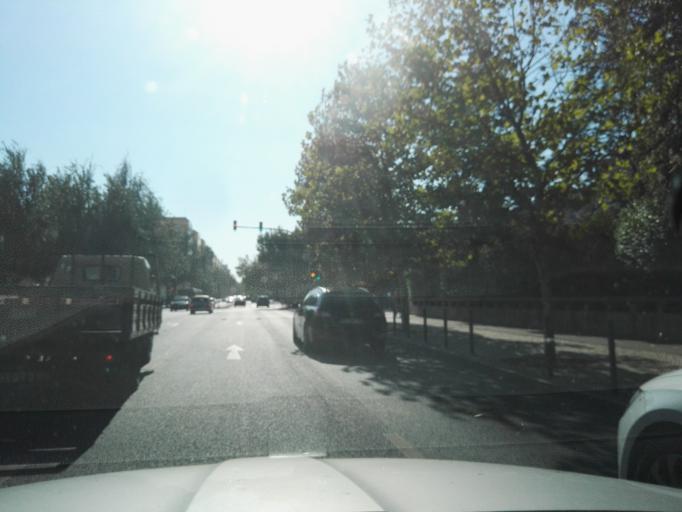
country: PT
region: Lisbon
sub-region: Odivelas
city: Olival do Basto
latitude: 38.7585
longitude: -9.1404
